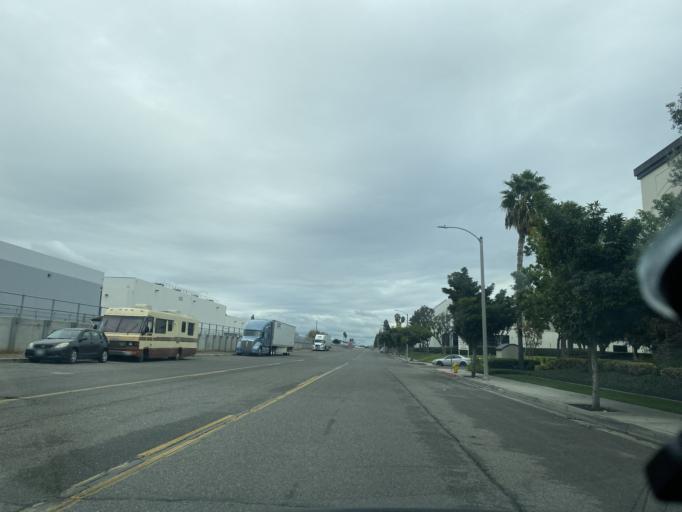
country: US
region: California
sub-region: Orange County
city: Fullerton
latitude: 33.8668
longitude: -117.9029
